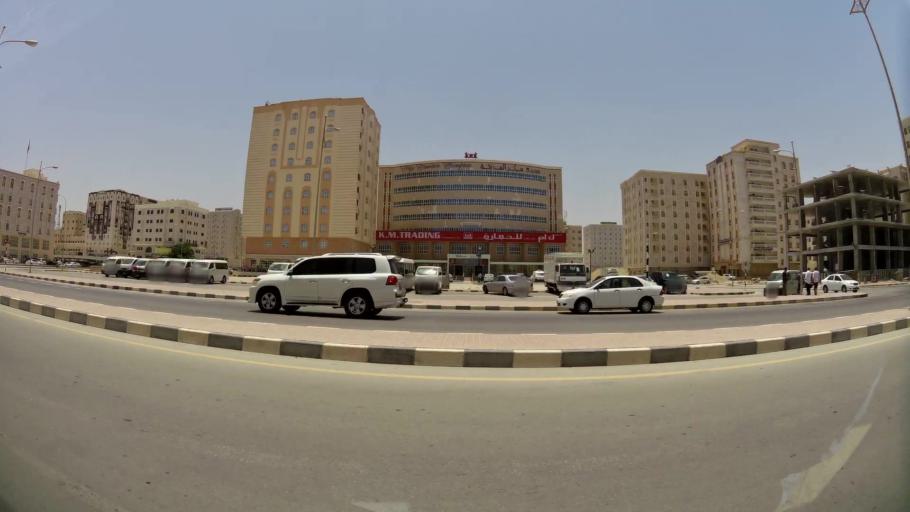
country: OM
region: Zufar
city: Salalah
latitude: 17.0185
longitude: 54.0954
